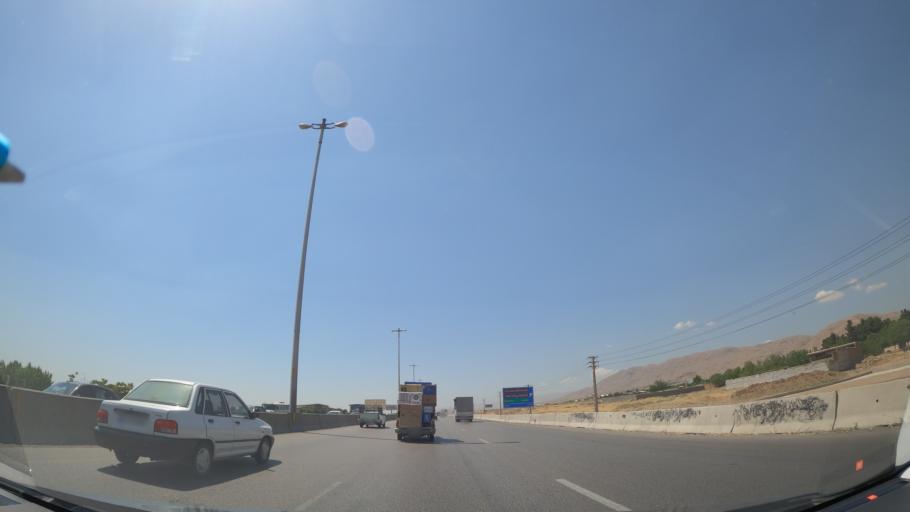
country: IR
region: Alborz
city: Karaj
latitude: 35.8735
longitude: 50.8943
